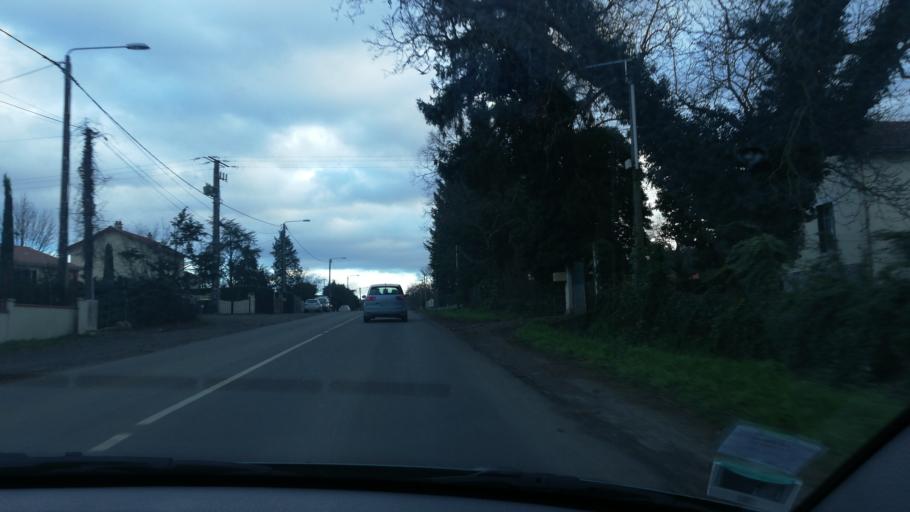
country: FR
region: Auvergne
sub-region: Departement du Puy-de-Dome
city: Vertaizon
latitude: 45.7813
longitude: 3.2888
